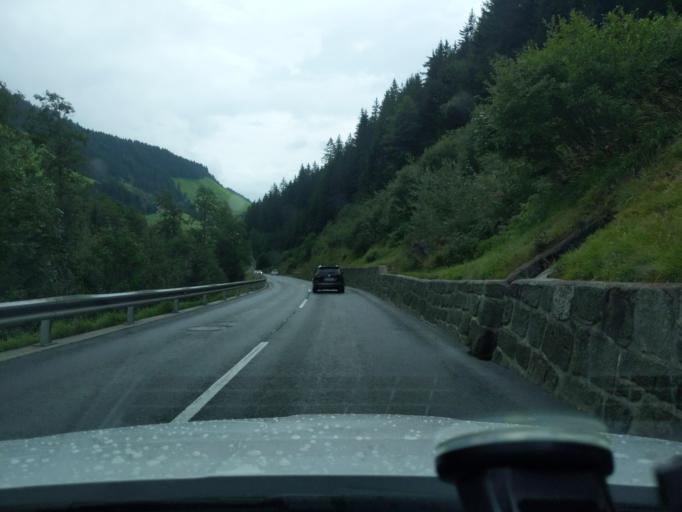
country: AT
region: Tyrol
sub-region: Politischer Bezirk Schwaz
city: Schwendau
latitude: 47.1598
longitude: 11.7537
